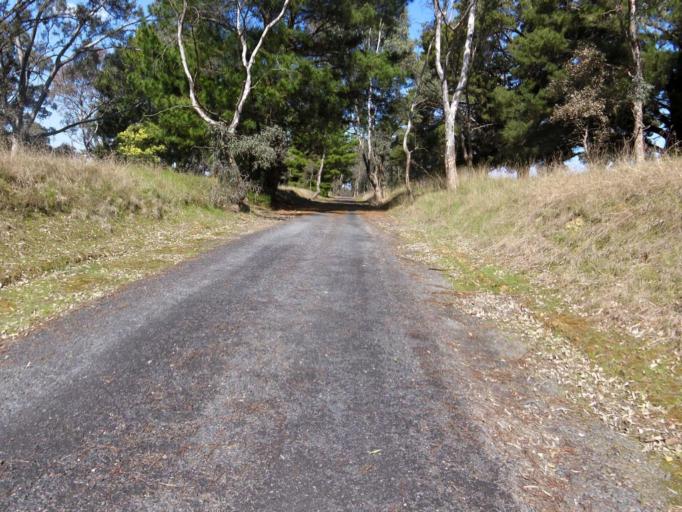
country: AU
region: Victoria
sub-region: Murrindindi
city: Alexandra
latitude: -36.9906
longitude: 145.7370
